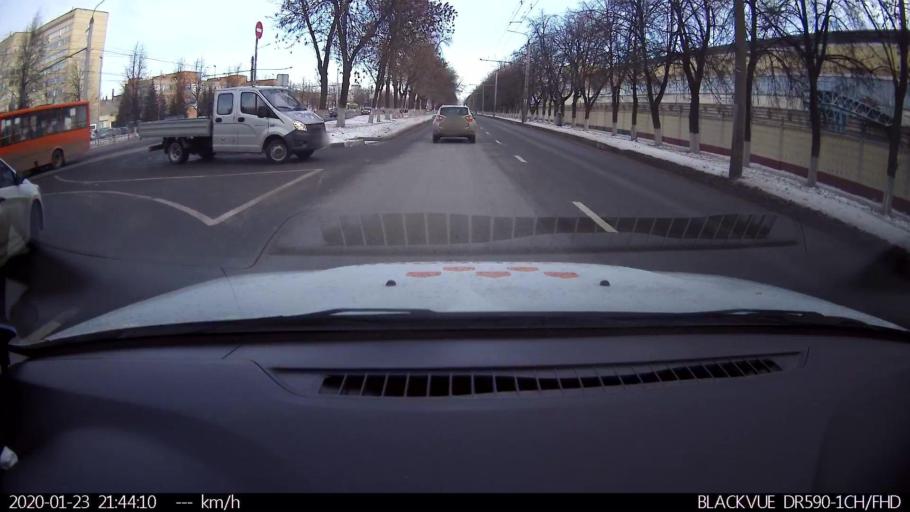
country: RU
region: Nizjnij Novgorod
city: Nizhniy Novgorod
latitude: 56.2543
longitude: 43.8932
